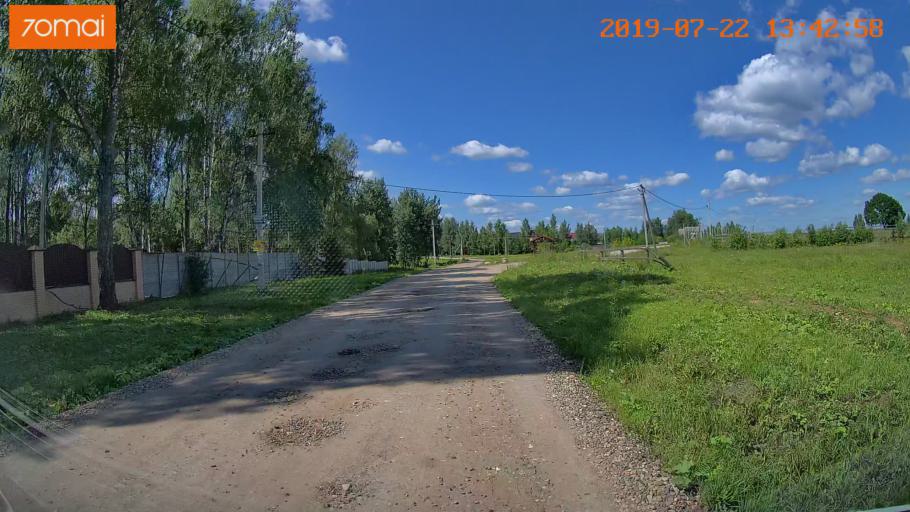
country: RU
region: Ivanovo
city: Novo-Talitsy
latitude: 57.0814
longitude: 40.8749
